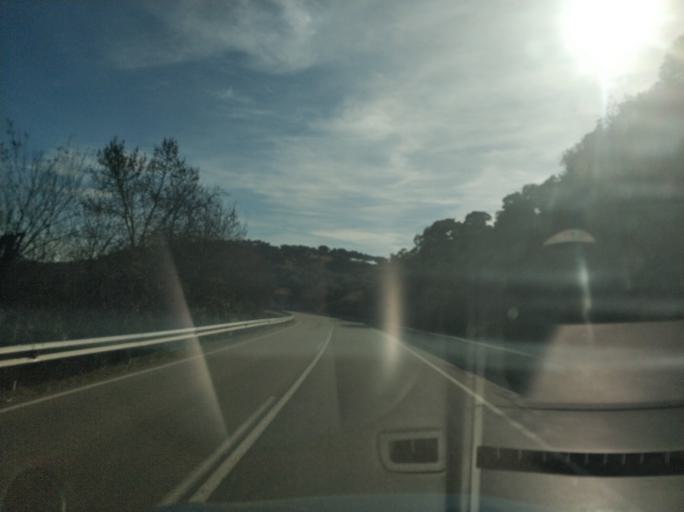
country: ES
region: Castille and Leon
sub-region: Provincia de Salamanca
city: Carrascal de Barregas
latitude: 40.9938
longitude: -5.7335
